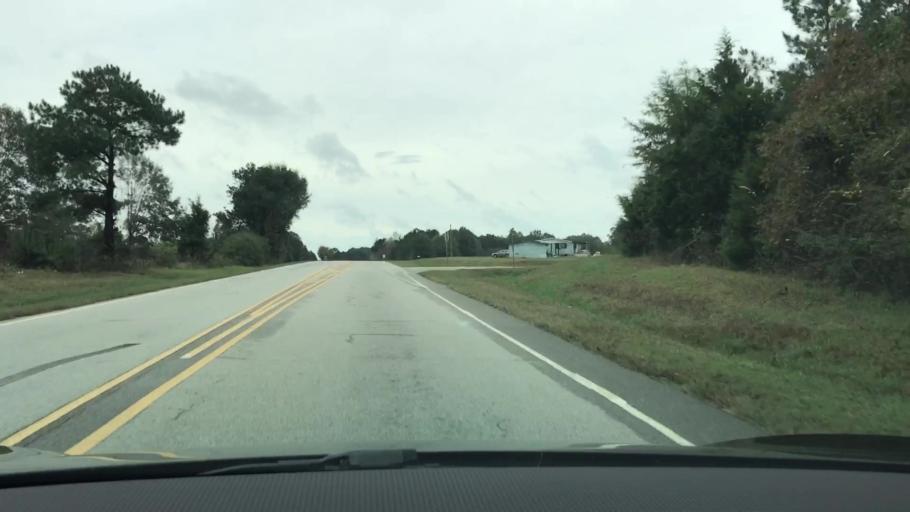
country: US
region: Georgia
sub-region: Taliaferro County
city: Crawfordville
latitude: 33.4930
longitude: -82.7999
